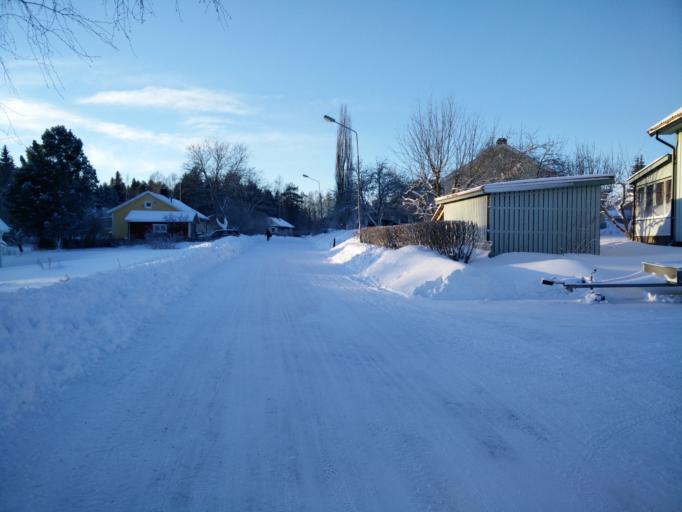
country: SE
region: Vaesternorrland
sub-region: Sundsvalls Kommun
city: Kvissleby
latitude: 62.2942
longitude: 17.3739
